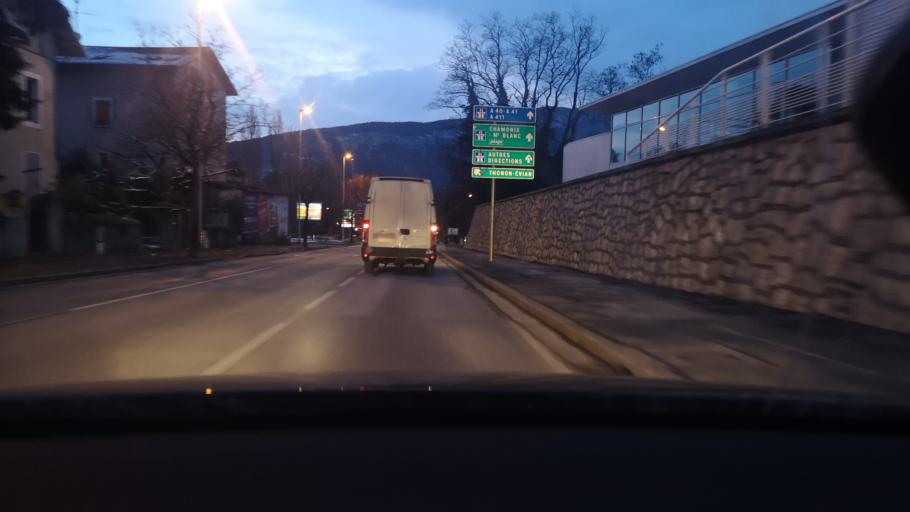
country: FR
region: Rhone-Alpes
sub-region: Departement de la Haute-Savoie
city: Annemasse
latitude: 46.1890
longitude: 6.2328
